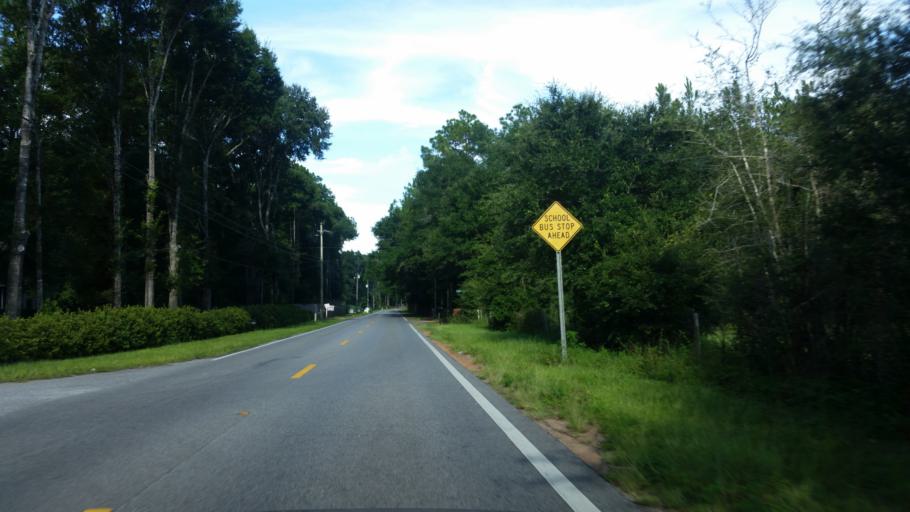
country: US
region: Florida
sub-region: Santa Rosa County
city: Milton
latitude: 30.6214
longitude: -87.0817
